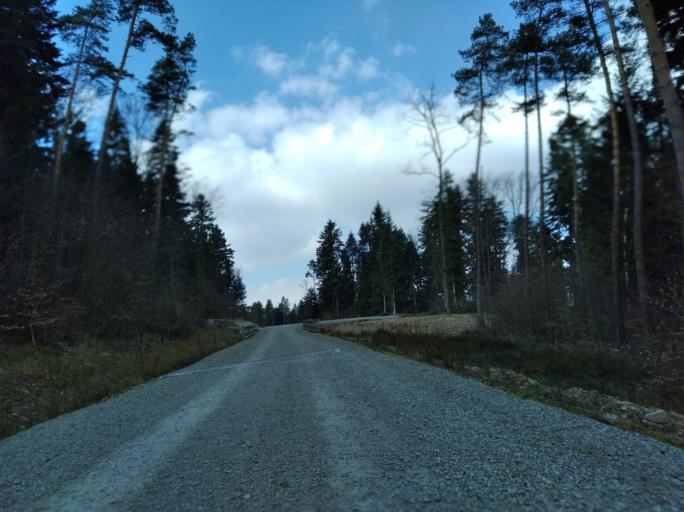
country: PL
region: Subcarpathian Voivodeship
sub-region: Powiat strzyzowski
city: Strzyzow
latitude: 49.8171
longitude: 21.8127
